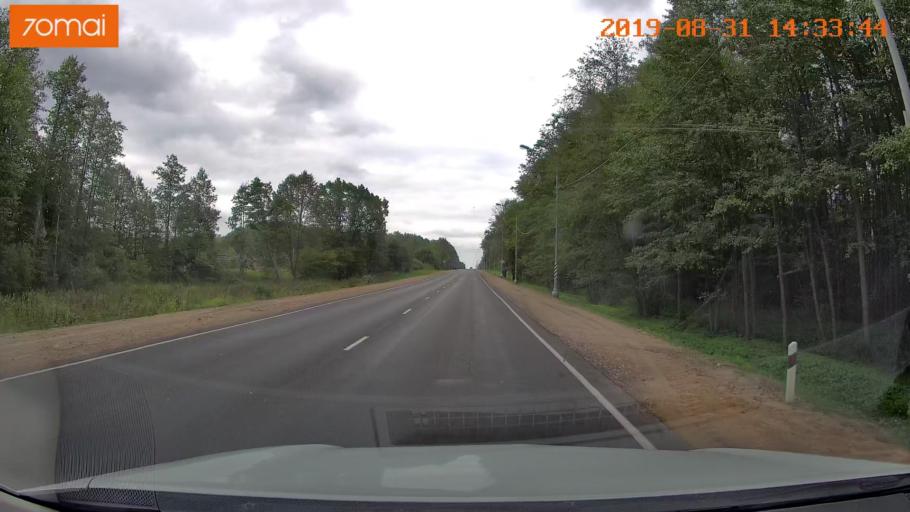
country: RU
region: Smolensk
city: Yekimovichi
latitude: 54.1537
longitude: 33.4251
